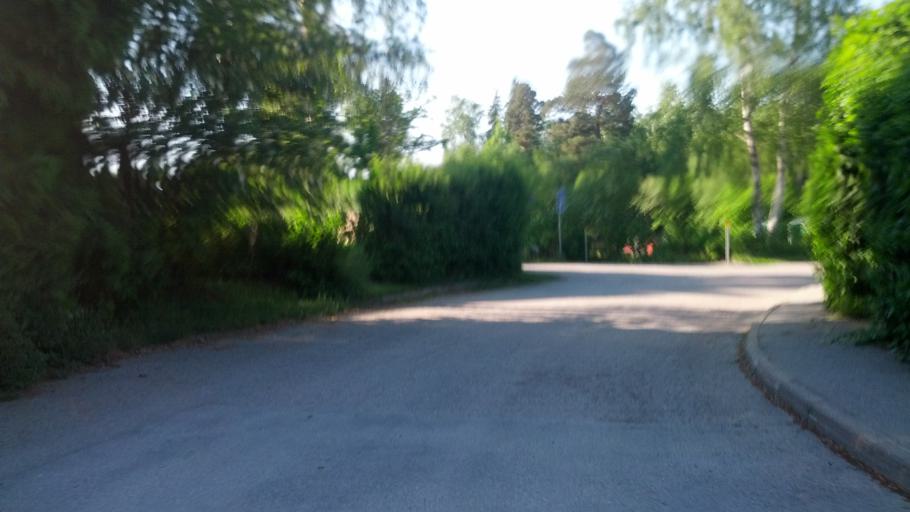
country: SE
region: Stockholm
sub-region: Vallentuna Kommun
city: Vallentuna
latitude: 59.5017
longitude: 18.0702
